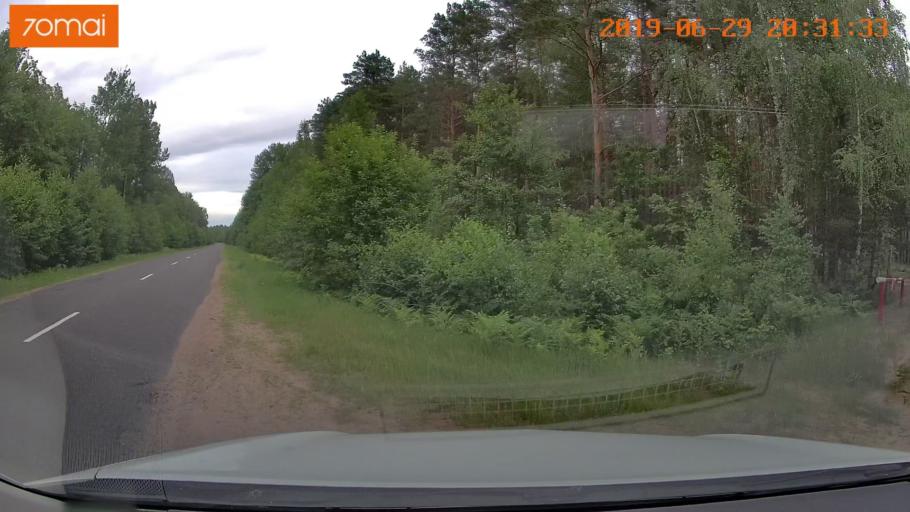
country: BY
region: Brest
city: Hantsavichy
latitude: 52.5143
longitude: 26.3449
